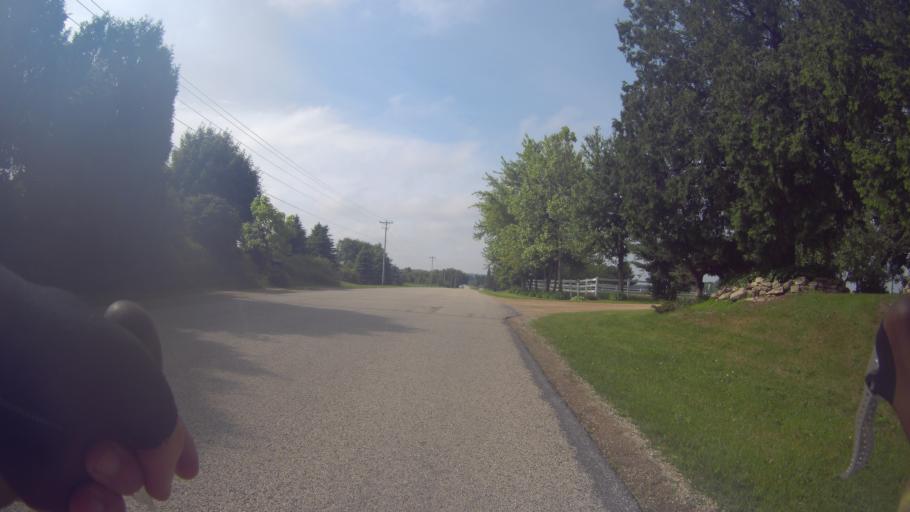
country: US
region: Wisconsin
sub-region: Dane County
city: McFarland
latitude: 43.0072
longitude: -89.2350
